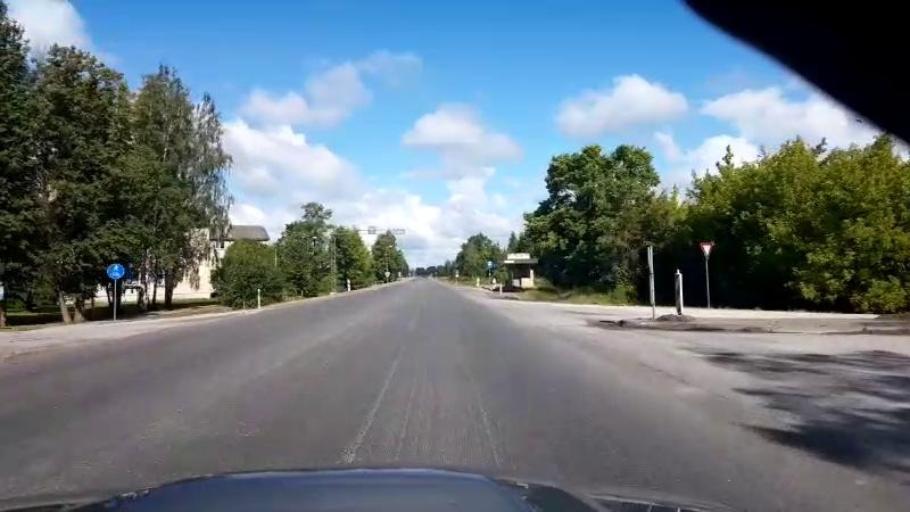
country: LV
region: Bauskas Rajons
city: Bauska
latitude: 56.3981
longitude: 24.2325
